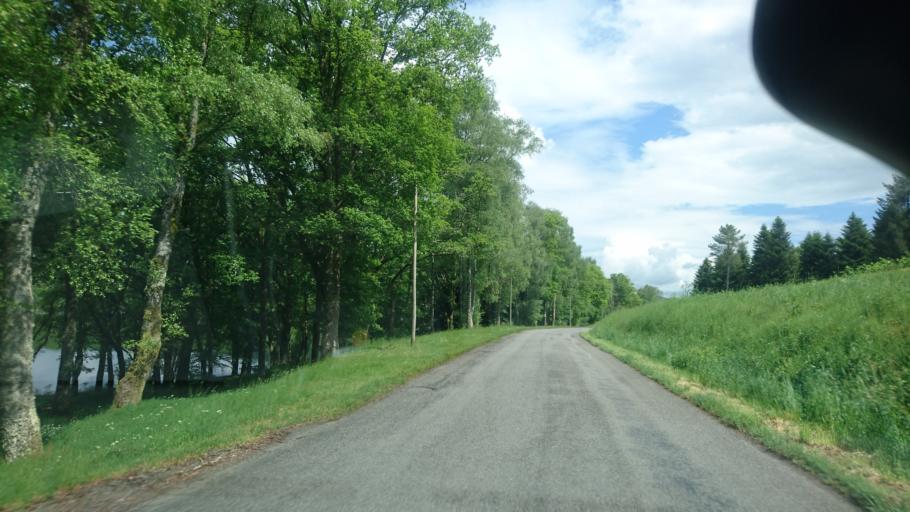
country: FR
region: Limousin
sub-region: Departement de la Haute-Vienne
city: Peyrat-le-Chateau
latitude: 45.7870
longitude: 1.8819
